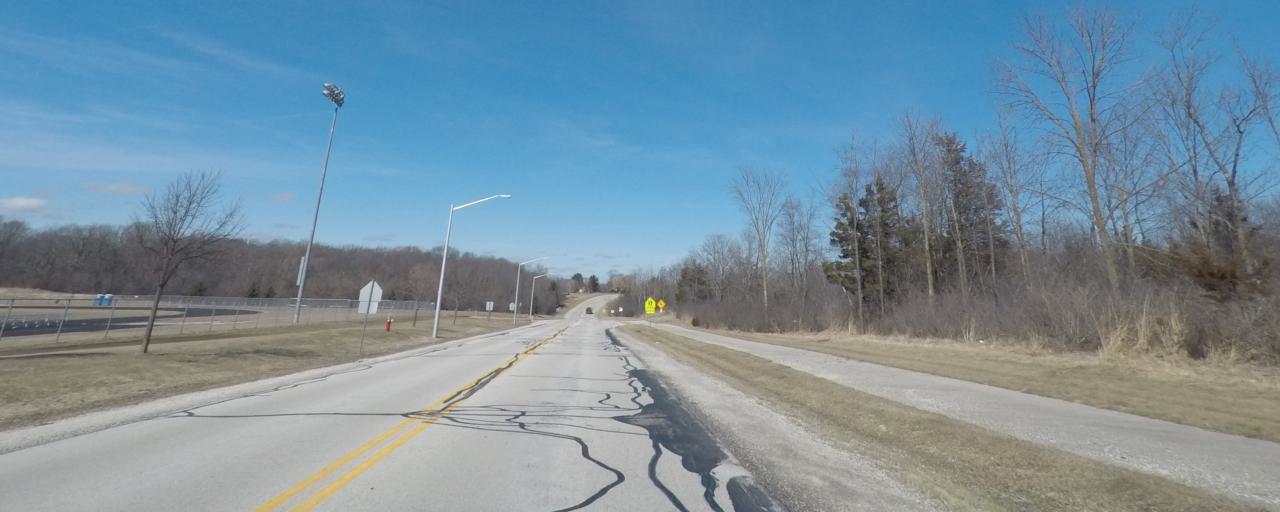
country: US
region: Wisconsin
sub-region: Waukesha County
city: Hartland
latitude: 43.1107
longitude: -88.3579
